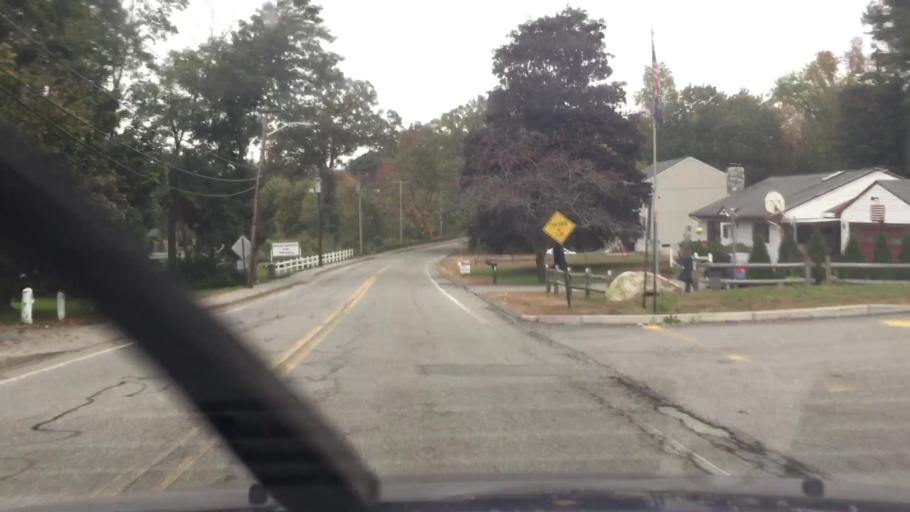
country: US
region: Massachusetts
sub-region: Middlesex County
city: Dracut
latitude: 42.6792
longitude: -71.3619
